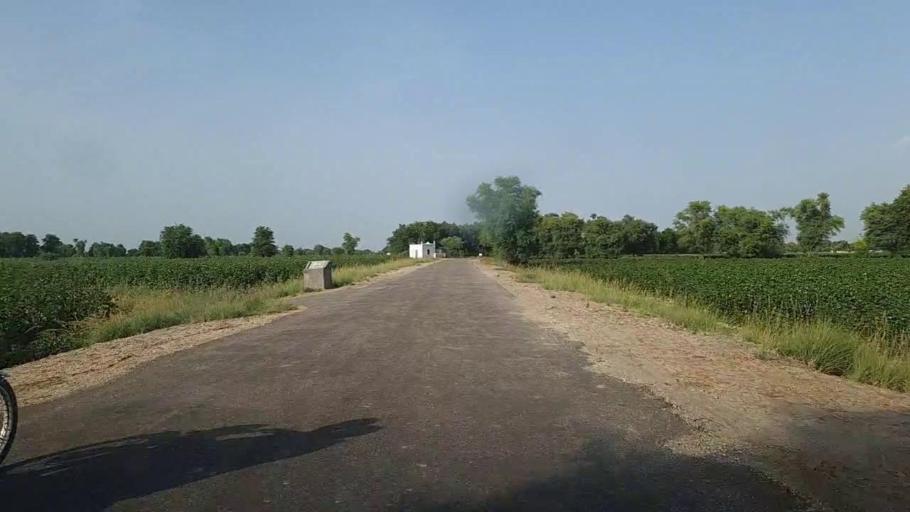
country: PK
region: Sindh
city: Ubauro
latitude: 28.0854
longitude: 69.8397
